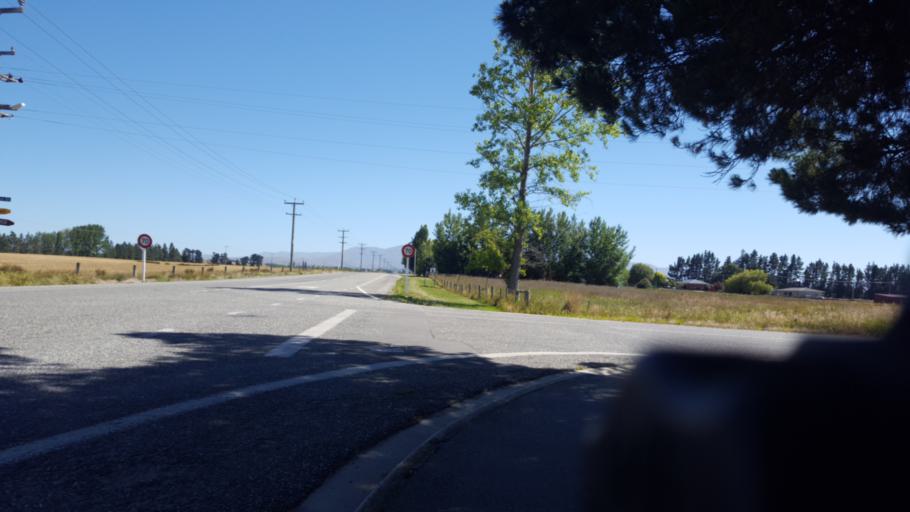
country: NZ
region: Otago
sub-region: Dunedin City
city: Dunedin
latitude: -45.1238
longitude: 170.0954
